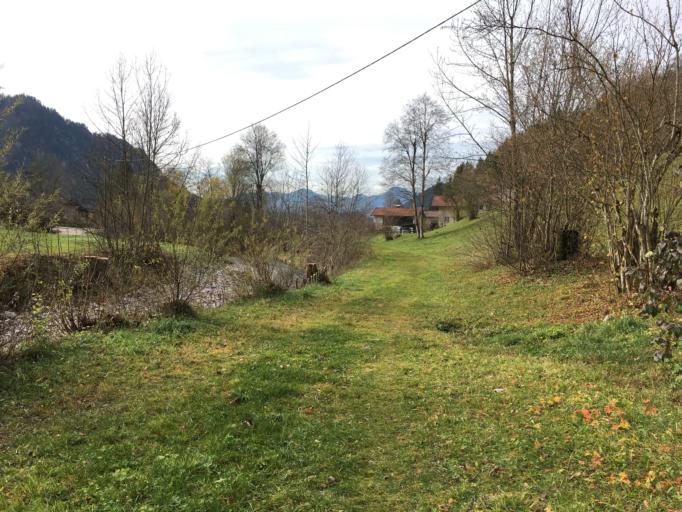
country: AT
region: Tyrol
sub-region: Politischer Bezirk Kufstein
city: Walchsee
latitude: 47.6617
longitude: 12.3232
